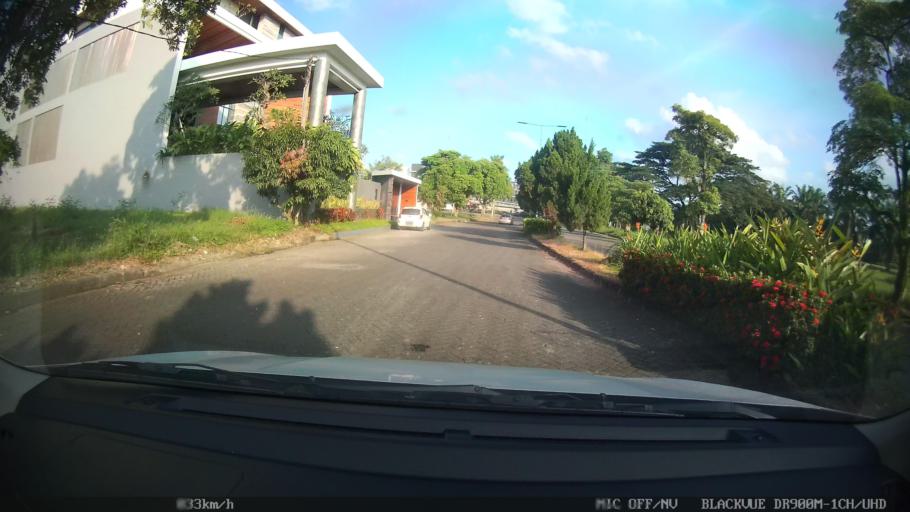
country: ID
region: North Sumatra
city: Medan
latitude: 3.6243
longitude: 98.6582
